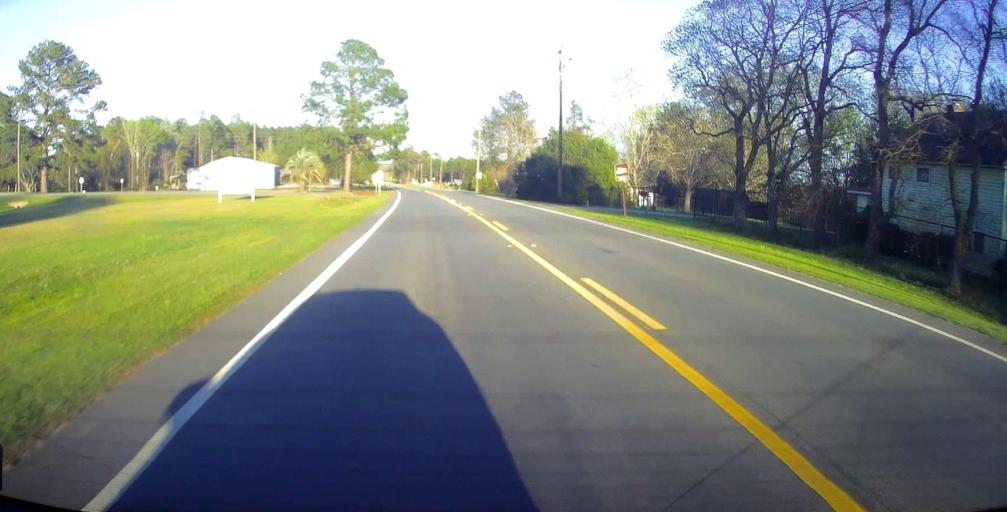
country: US
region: Georgia
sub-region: Wilcox County
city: Abbeville
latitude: 31.9925
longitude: -83.3030
